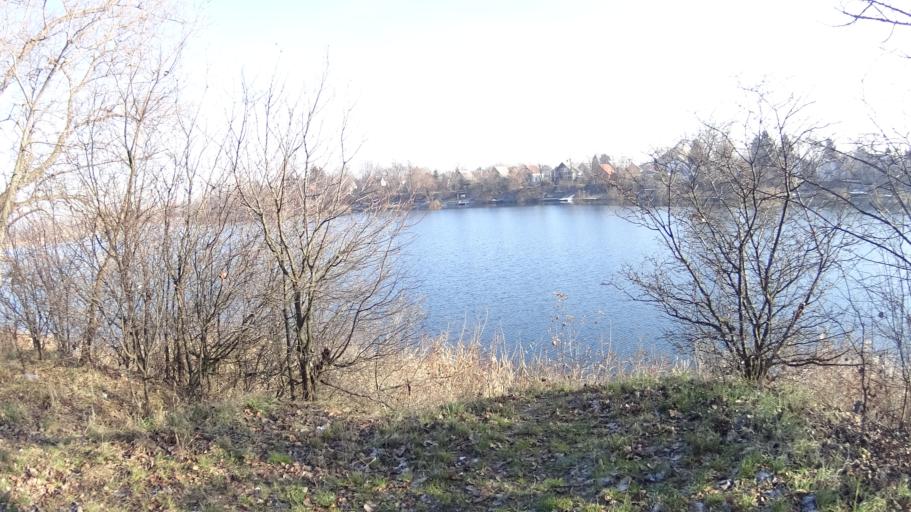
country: HU
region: Borsod-Abauj-Zemplen
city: Nyekladhaza
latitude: 47.9877
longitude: 20.8508
